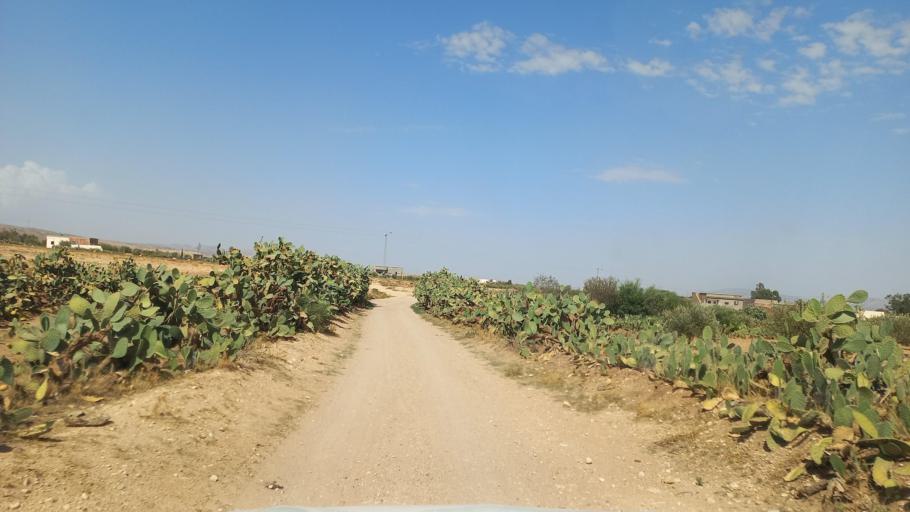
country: TN
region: Al Qasrayn
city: Kasserine
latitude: 35.2774
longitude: 8.9528
